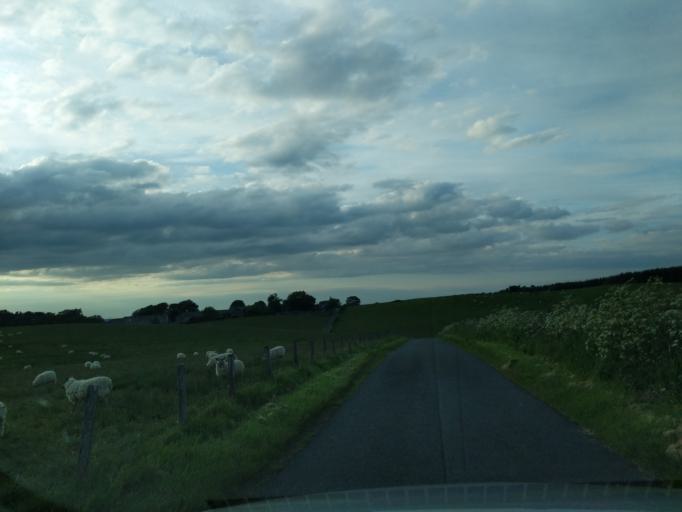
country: GB
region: Scotland
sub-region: Midlothian
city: Gorebridge
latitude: 55.7935
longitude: -3.0919
